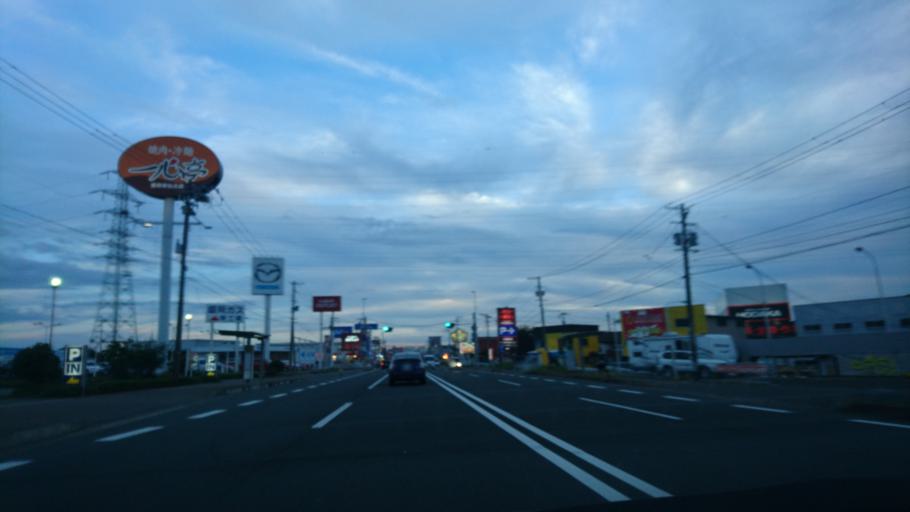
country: JP
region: Iwate
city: Morioka-shi
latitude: 39.6794
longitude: 141.1558
